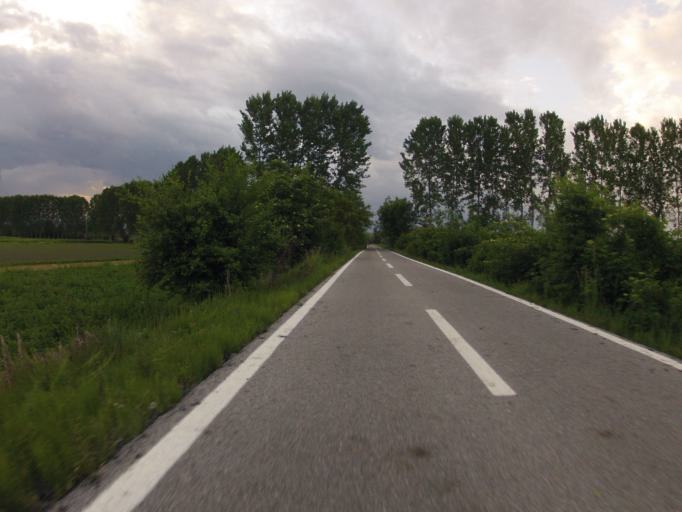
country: IT
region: Piedmont
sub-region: Provincia di Torino
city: Vigone
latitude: 44.8267
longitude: 7.4945
